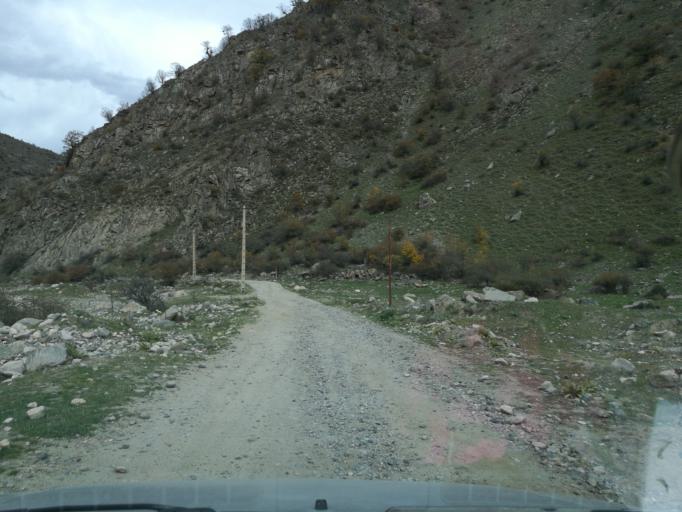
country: IR
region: Mazandaran
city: `Abbasabad
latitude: 36.4351
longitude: 51.0454
